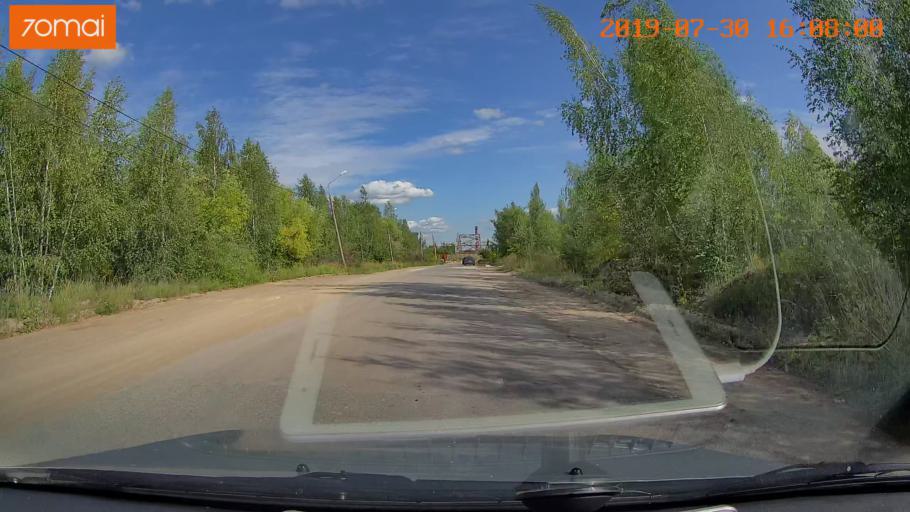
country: RU
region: Moskovskaya
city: Peski
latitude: 55.2477
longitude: 38.7250
